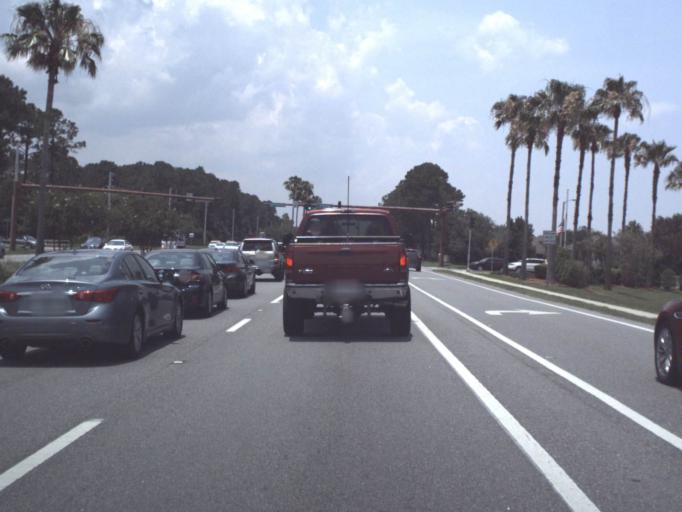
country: US
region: Florida
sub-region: Saint Johns County
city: Ponte Vedra Beach
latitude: 30.2158
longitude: -81.3810
